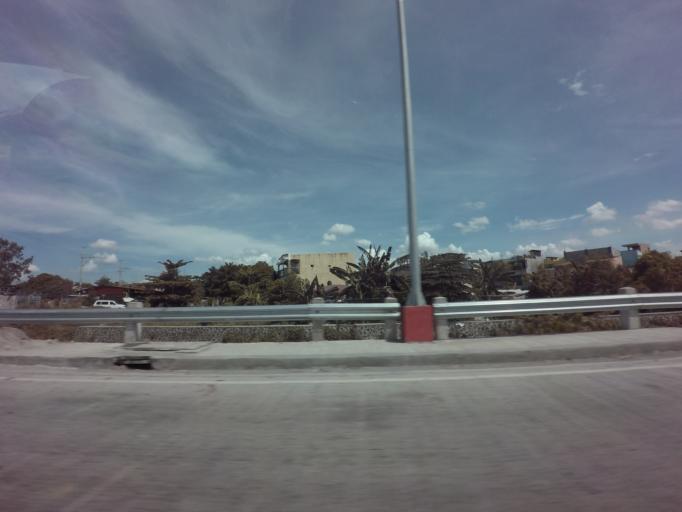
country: PH
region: Calabarzon
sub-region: Province of Rizal
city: Taguig
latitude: 14.5172
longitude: 121.0763
